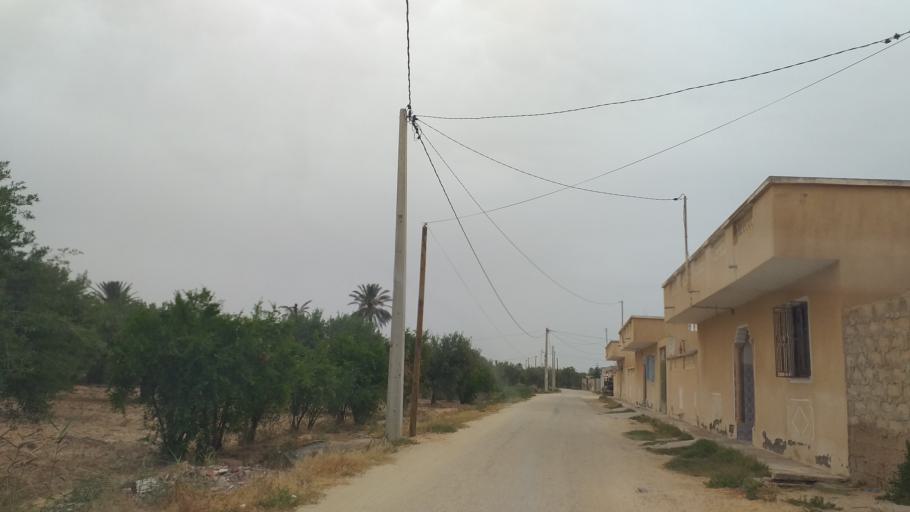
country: TN
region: Qabis
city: Gabes
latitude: 33.9506
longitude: 10.0607
